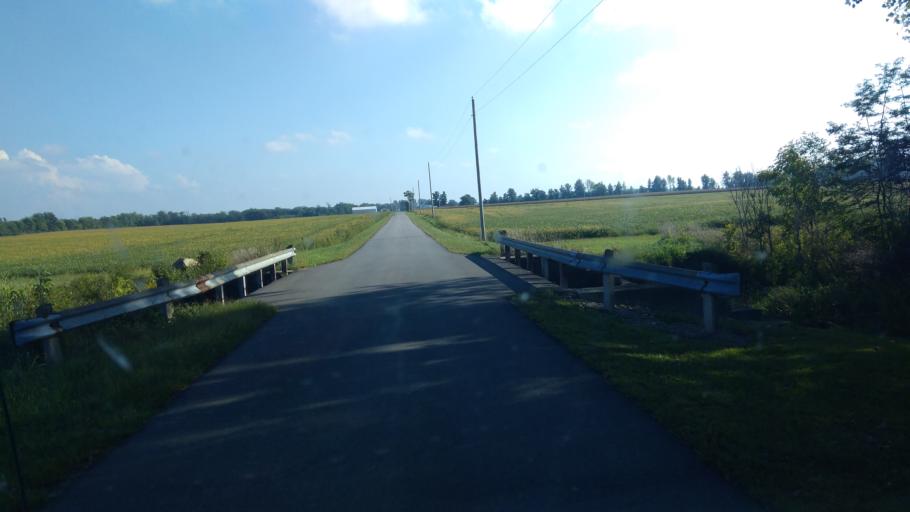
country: US
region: Ohio
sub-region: Hardin County
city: Forest
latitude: 40.7267
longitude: -83.4779
